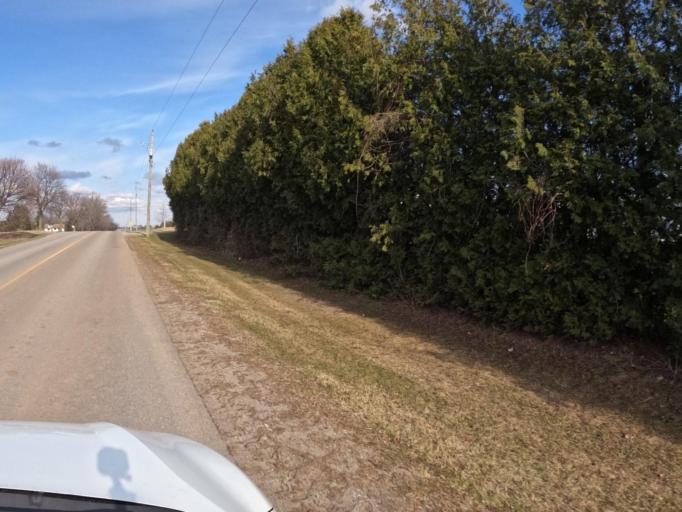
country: CA
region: Ontario
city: Brant
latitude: 43.0077
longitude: -80.3953
